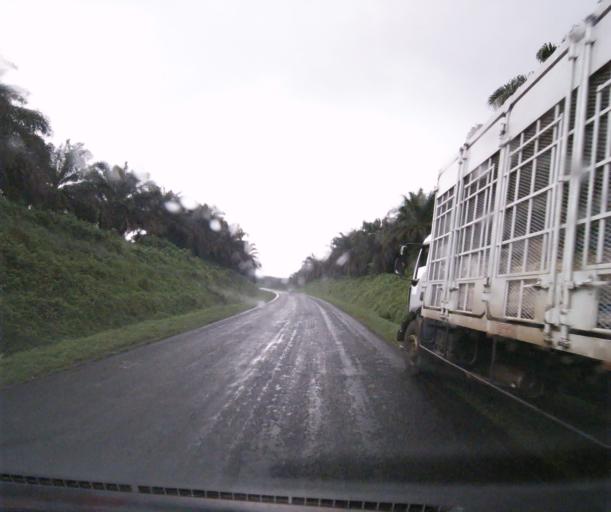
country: CM
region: South-West Province
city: Idenao
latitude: 4.1239
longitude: 8.9901
